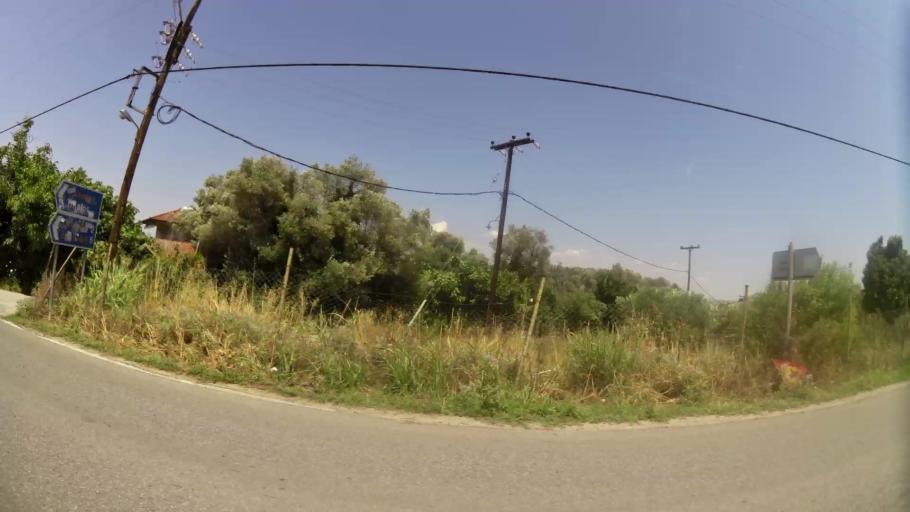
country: GR
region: Central Macedonia
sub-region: Nomos Thessalonikis
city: Trilofos
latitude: 40.4717
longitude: 22.9734
